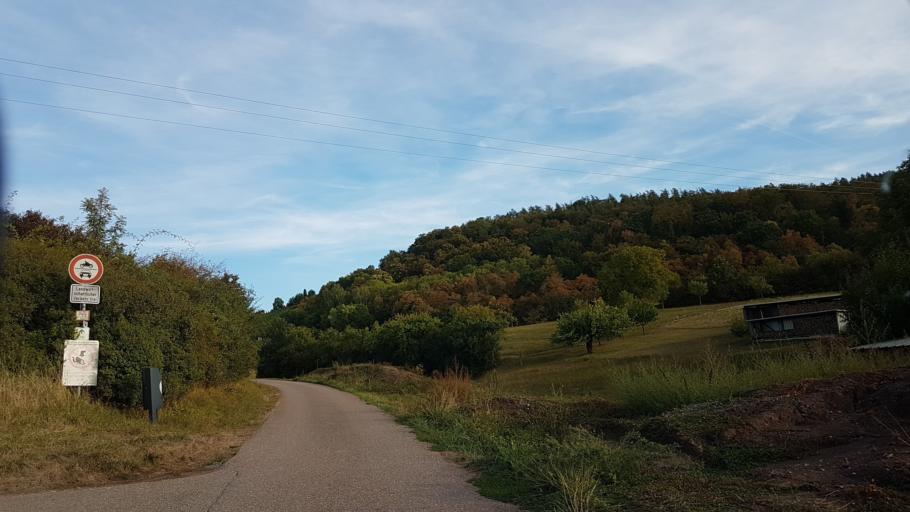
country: DE
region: Baden-Wuerttemberg
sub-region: Regierungsbezirk Stuttgart
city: Neuenstadt am Kocher
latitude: 49.2136
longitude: 9.3620
